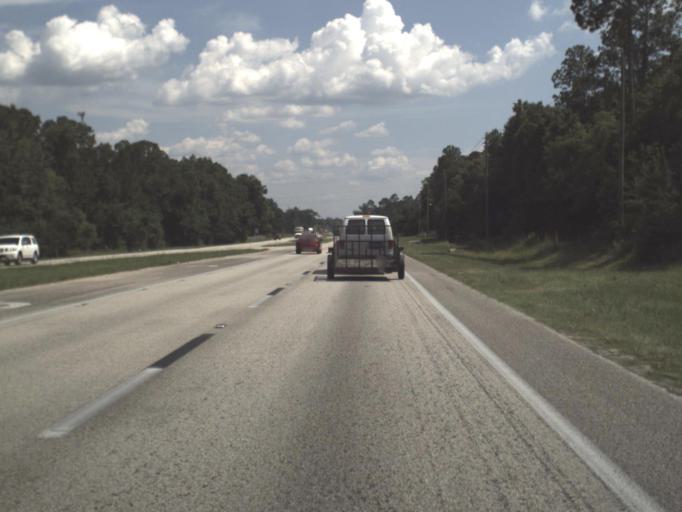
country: US
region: Florida
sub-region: Alachua County
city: Waldo
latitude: 29.8051
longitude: -82.1678
